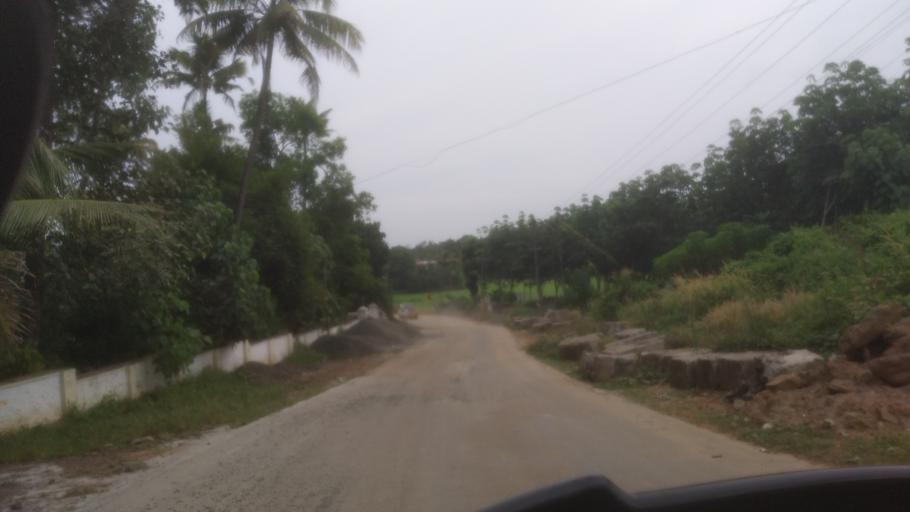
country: IN
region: Kerala
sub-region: Ernakulam
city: Perumbavoor
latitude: 10.0482
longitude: 76.5270
